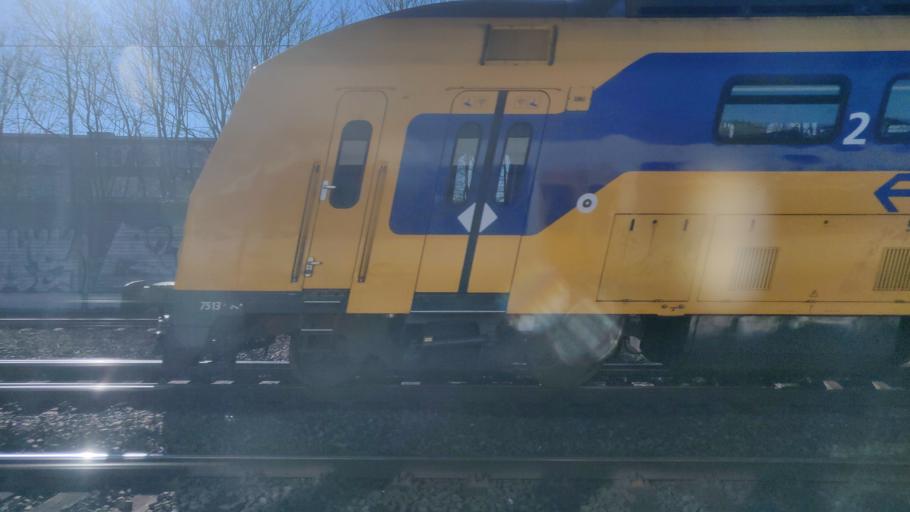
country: NL
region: North Holland
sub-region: Gemeente Weesp
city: Weesp
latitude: 52.3153
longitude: 5.0384
